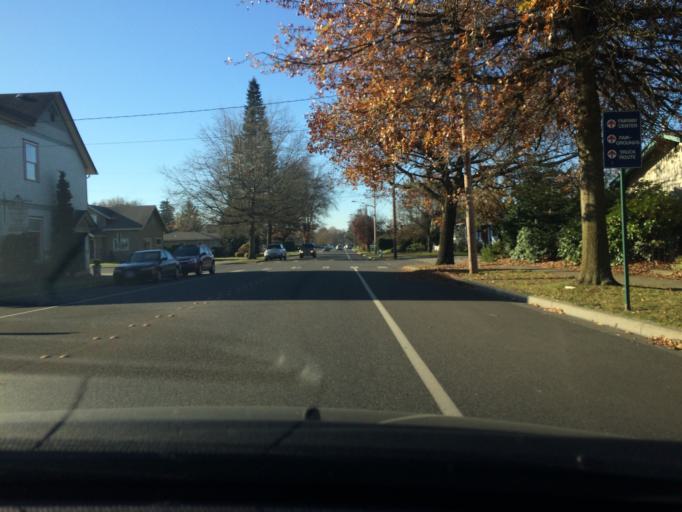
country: US
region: Washington
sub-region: Whatcom County
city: Lynden
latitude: 48.9429
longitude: -122.4568
